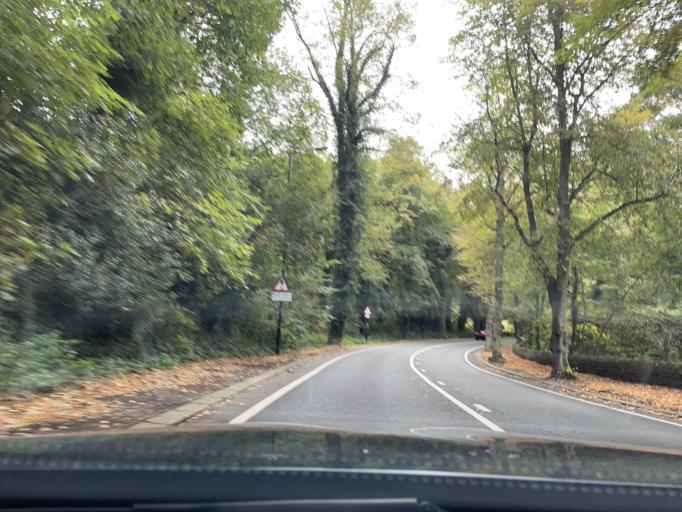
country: GB
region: England
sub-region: Sheffield
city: Oughtibridge
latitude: 53.3912
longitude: -1.5175
